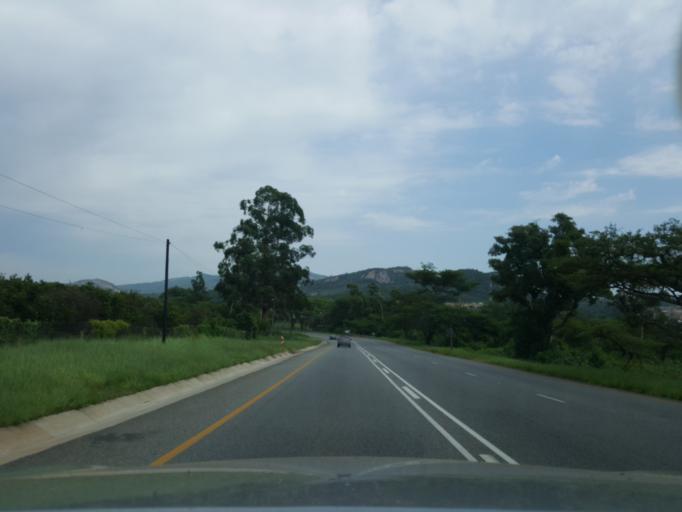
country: ZA
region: Mpumalanga
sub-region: Ehlanzeni District
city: Nelspruit
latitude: -25.4759
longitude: 31.1051
